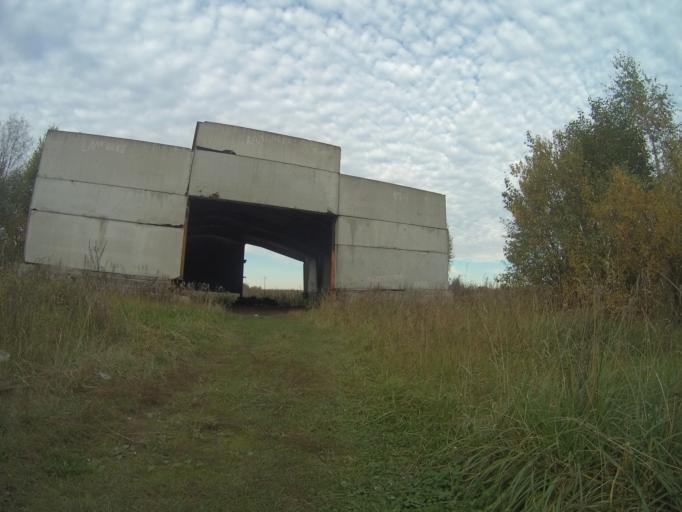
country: RU
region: Vladimir
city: Golovino
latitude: 55.9642
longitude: 40.4220
